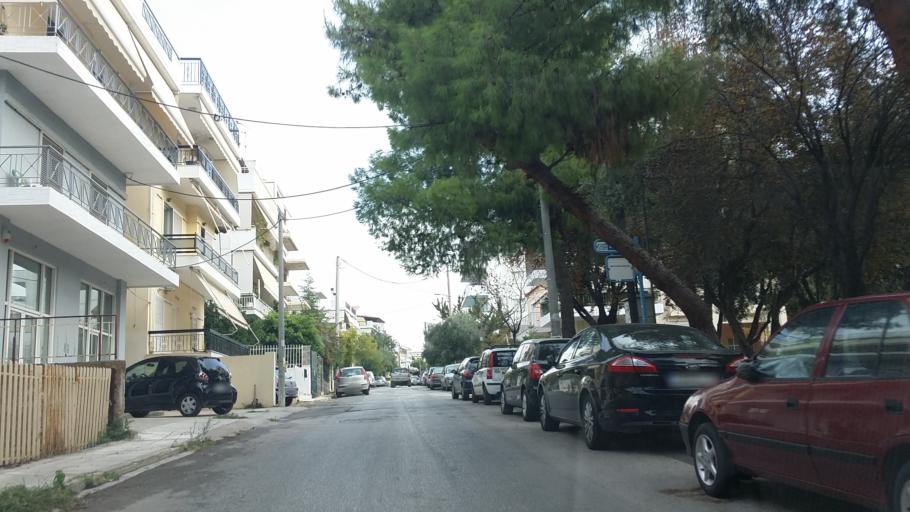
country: GR
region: Attica
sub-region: Nomarchia Athinas
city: Irakleio
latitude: 38.0556
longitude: 23.7566
